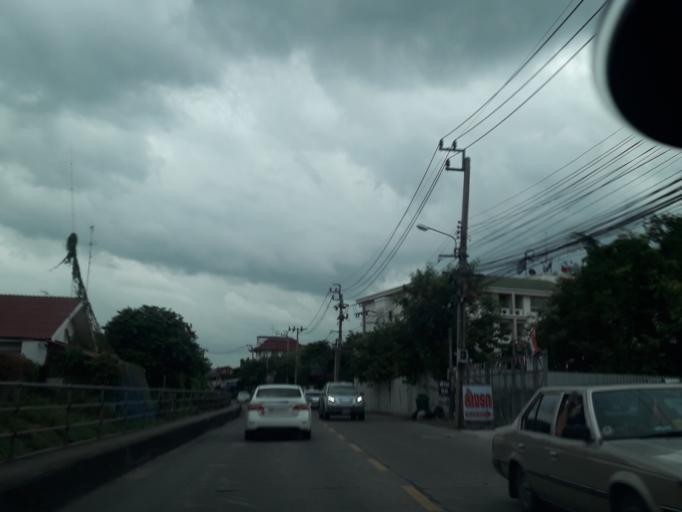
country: TH
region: Bangkok
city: Don Mueang
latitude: 13.9423
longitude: 100.6100
